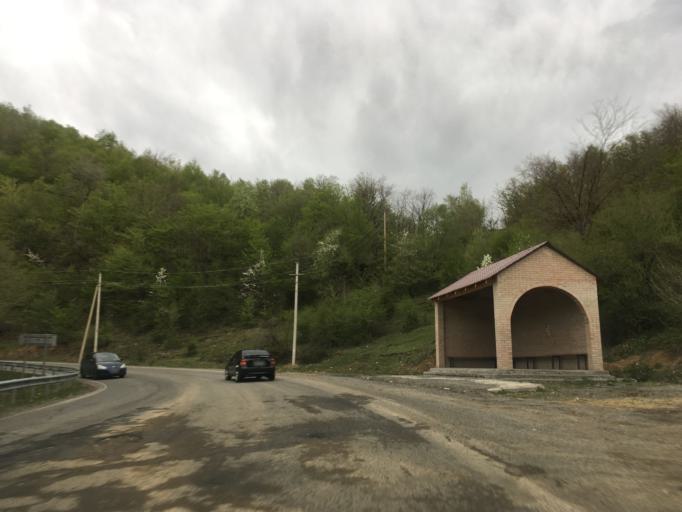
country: GE
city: Surami
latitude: 42.2142
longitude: 43.5437
